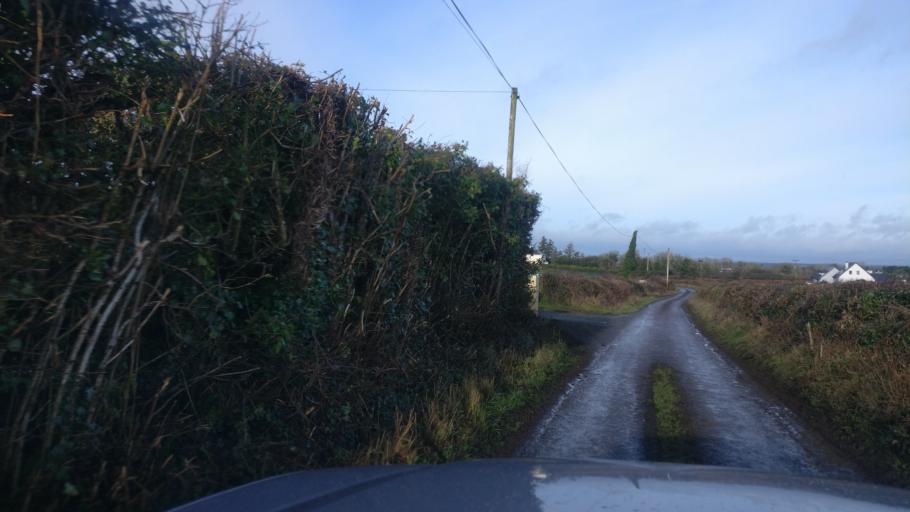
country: IE
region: Connaught
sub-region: County Galway
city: Loughrea
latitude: 53.2035
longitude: -8.6730
